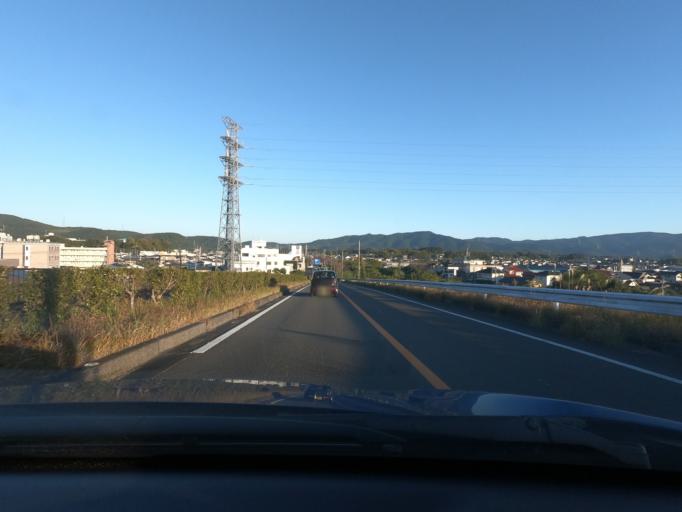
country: JP
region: Kagoshima
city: Satsumasendai
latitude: 31.8106
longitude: 130.3137
